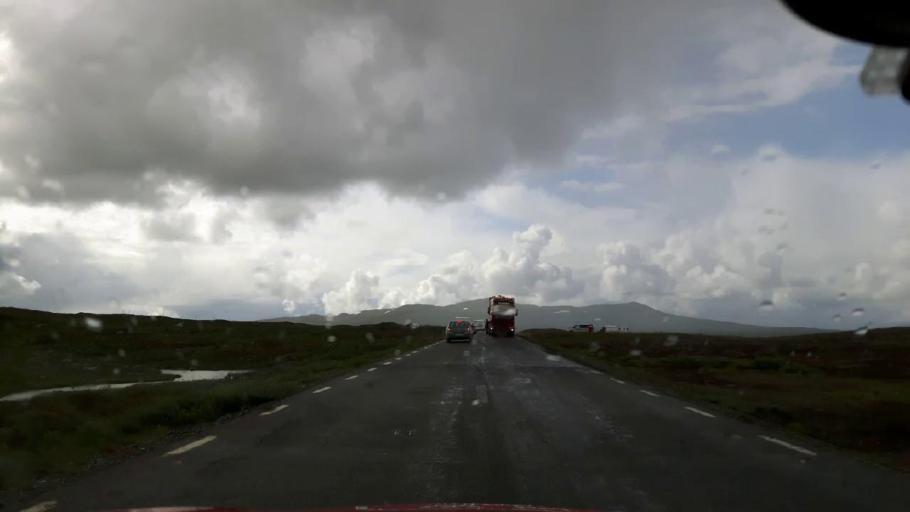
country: NO
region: Nordland
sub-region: Hattfjelldal
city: Hattfjelldal
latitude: 65.0943
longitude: 14.4649
